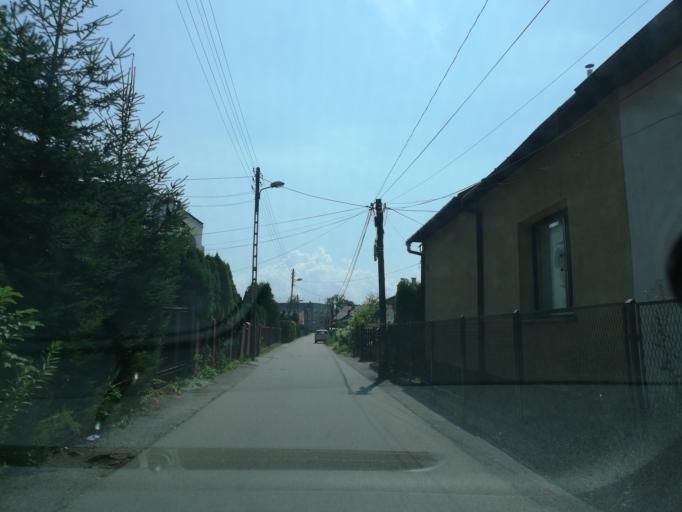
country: PL
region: Lesser Poland Voivodeship
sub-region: Powiat nowosadecki
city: Chelmiec
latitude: 49.6308
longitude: 20.6797
